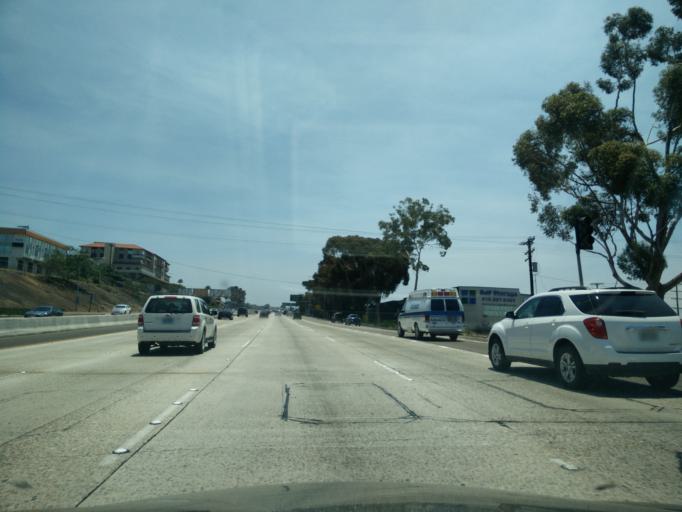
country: US
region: California
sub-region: San Diego County
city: San Diego
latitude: 32.7470
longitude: -117.1924
